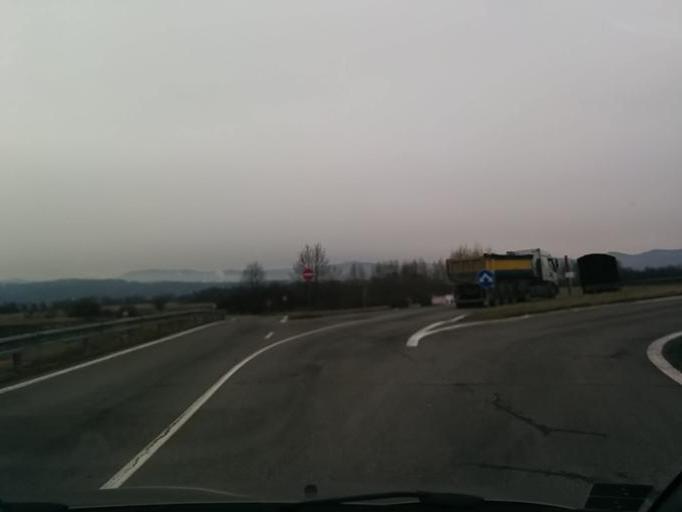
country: SK
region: Banskobystricky
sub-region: Okres Banska Bystrica
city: Zvolen
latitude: 48.6288
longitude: 19.1206
